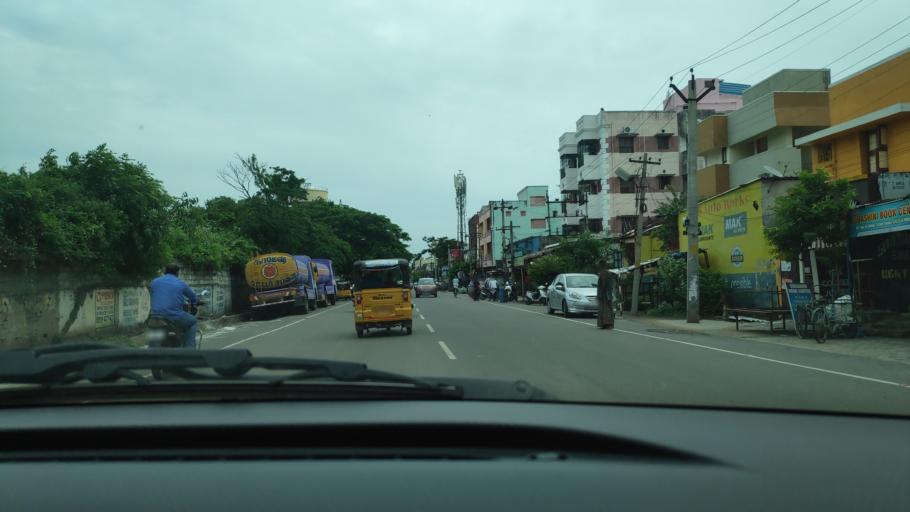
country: IN
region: Tamil Nadu
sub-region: Kancheepuram
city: Pallavaram
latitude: 12.9275
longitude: 80.1268
